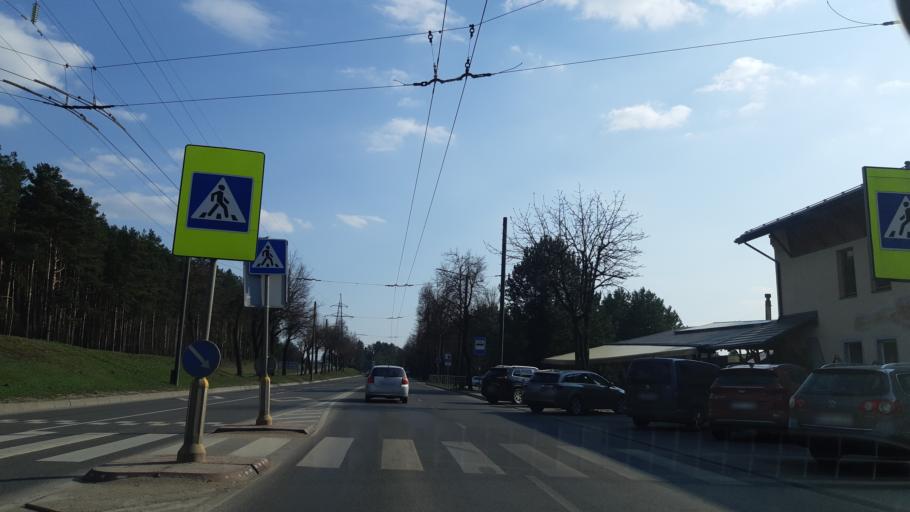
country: LT
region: Kauno apskritis
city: Dainava (Kaunas)
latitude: 54.8844
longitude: 24.0074
